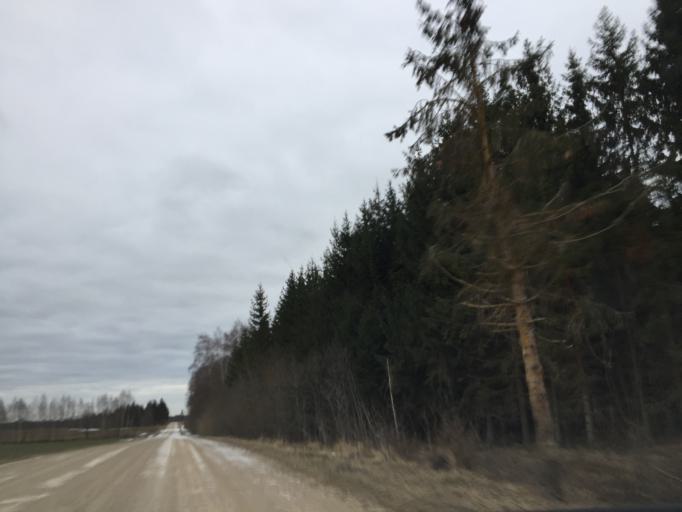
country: LT
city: Zagare
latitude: 56.3053
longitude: 23.2576
